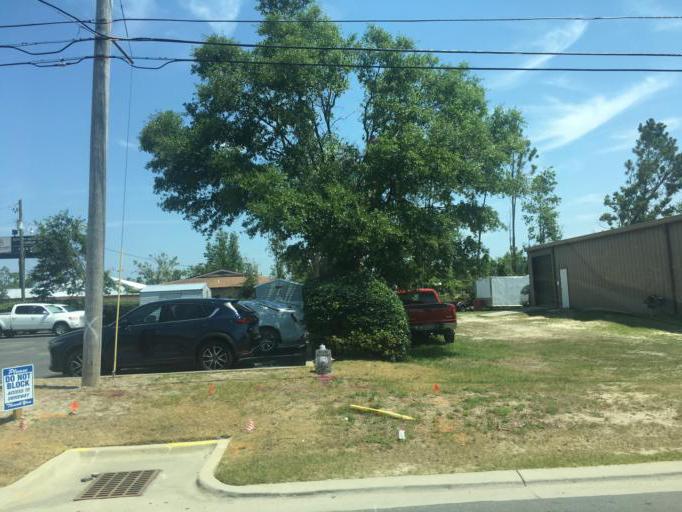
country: US
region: Florida
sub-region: Bay County
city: Hiland Park
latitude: 30.2113
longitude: -85.6488
